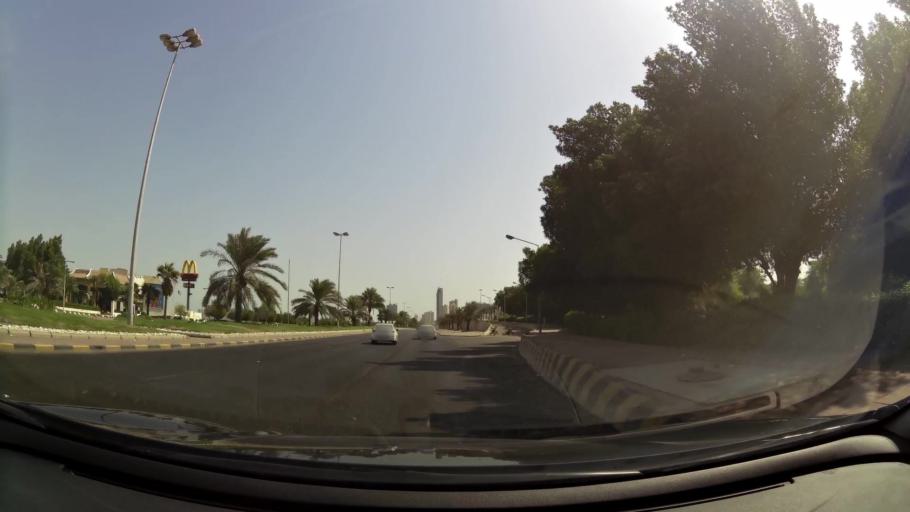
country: KW
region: Muhafazat Hawalli
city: Hawalli
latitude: 29.3492
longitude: 48.0350
